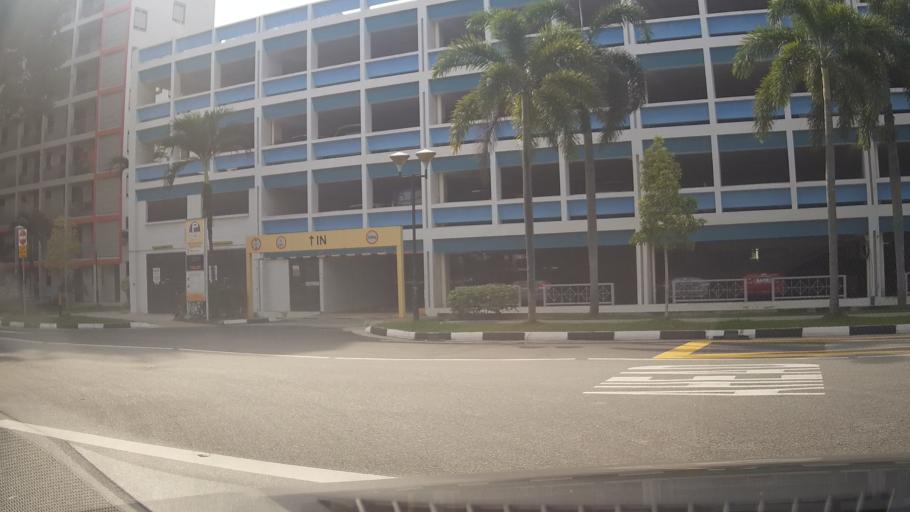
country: SG
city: Singapore
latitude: 1.3092
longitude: 103.8876
